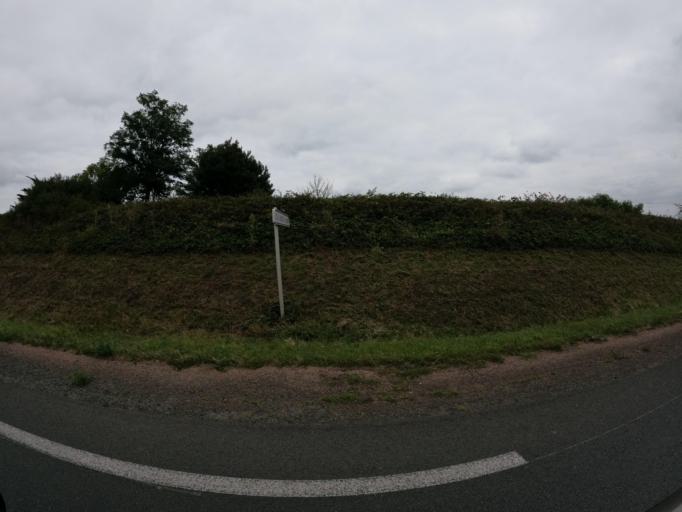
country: FR
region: Pays de la Loire
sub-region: Departement de la Vendee
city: Fontenay-le-Comte
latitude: 46.4664
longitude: -0.8463
